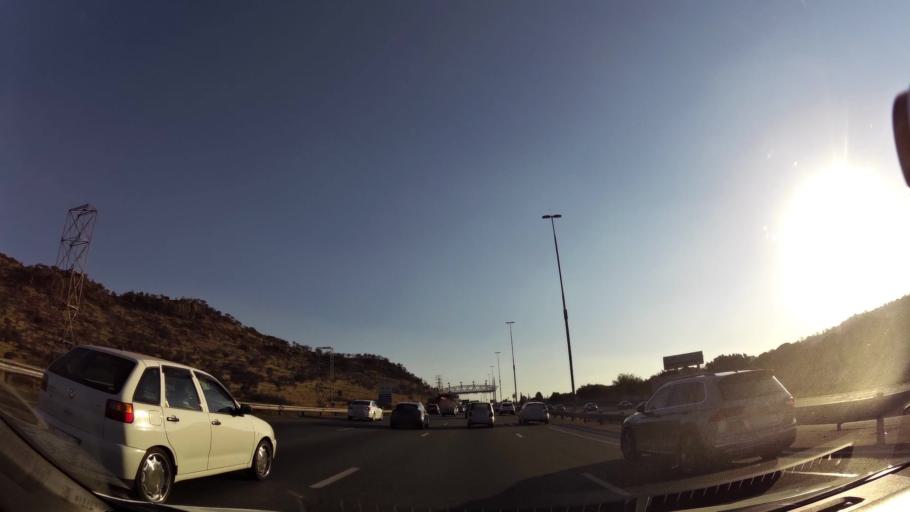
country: ZA
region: Gauteng
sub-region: City of Johannesburg Metropolitan Municipality
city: Johannesburg
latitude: -26.2663
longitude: 28.0746
